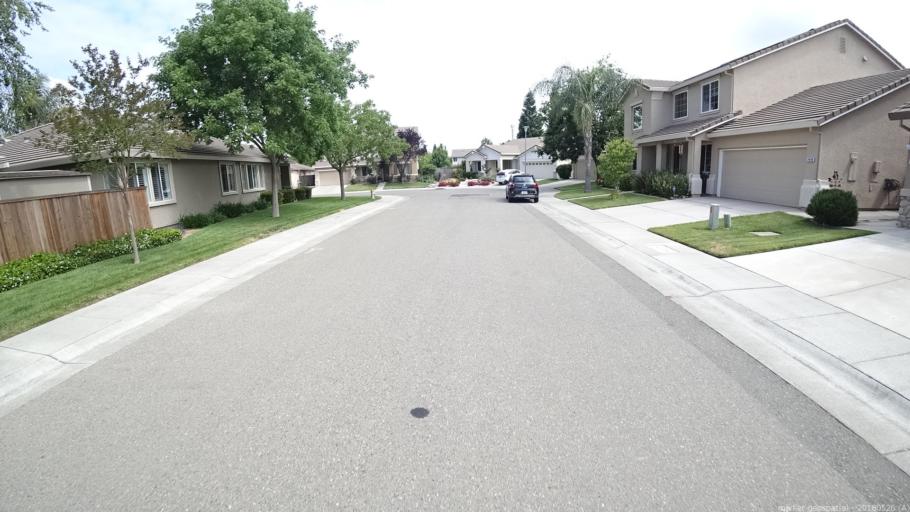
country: US
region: California
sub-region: Yolo County
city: West Sacramento
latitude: 38.6105
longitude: -121.5307
